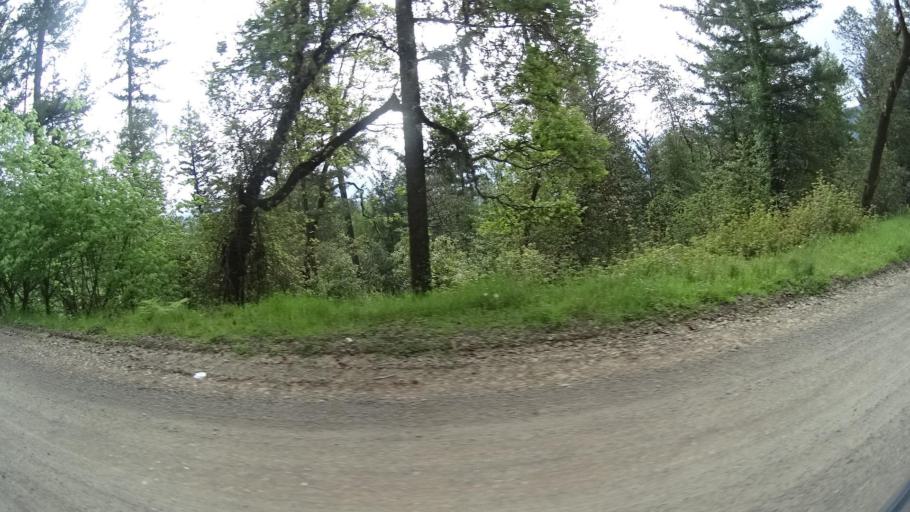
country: US
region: California
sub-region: Humboldt County
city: Redway
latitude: 40.2515
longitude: -123.7655
